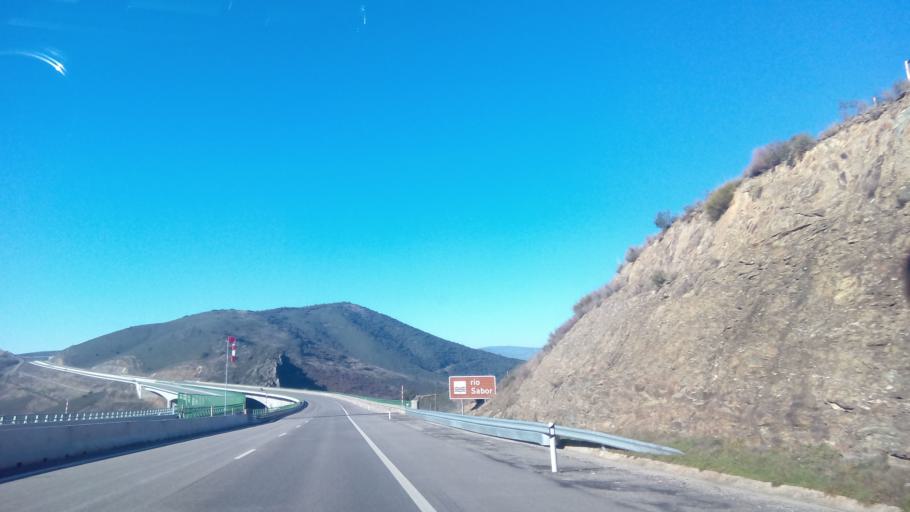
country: PT
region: Braganca
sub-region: Braganca Municipality
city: Braganca
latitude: 41.7736
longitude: -6.6738
